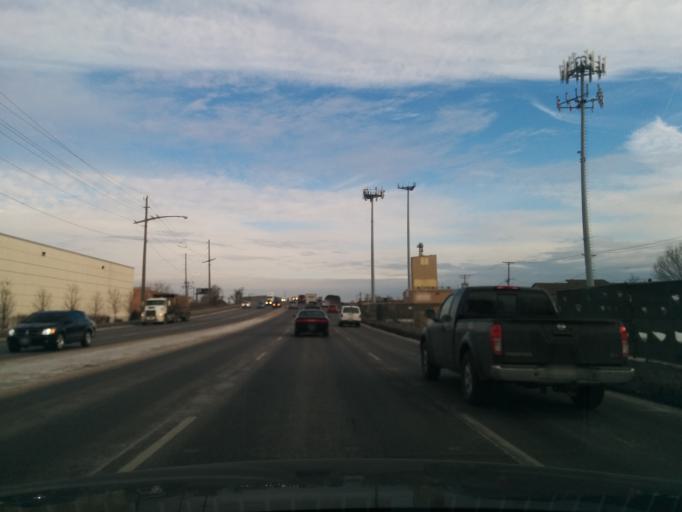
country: US
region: Illinois
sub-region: Cook County
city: Franklin Park
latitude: 41.9384
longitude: -87.8850
